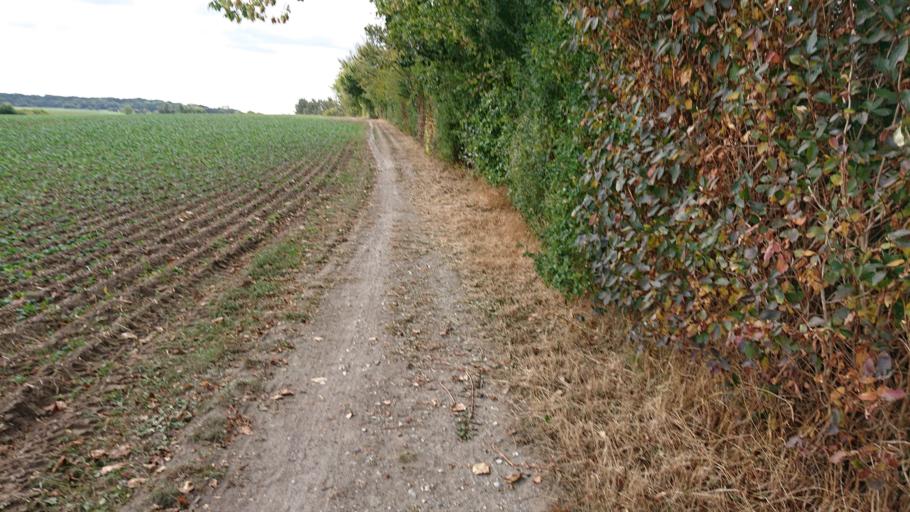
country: DE
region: Mecklenburg-Vorpommern
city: Altefahr
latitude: 54.3451
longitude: 13.1168
